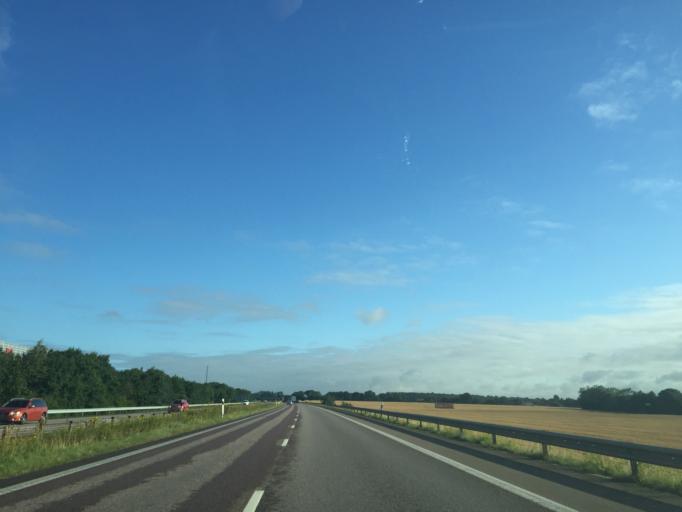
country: SE
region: Skane
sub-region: Helsingborg
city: Barslov
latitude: 56.0333
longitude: 12.7861
